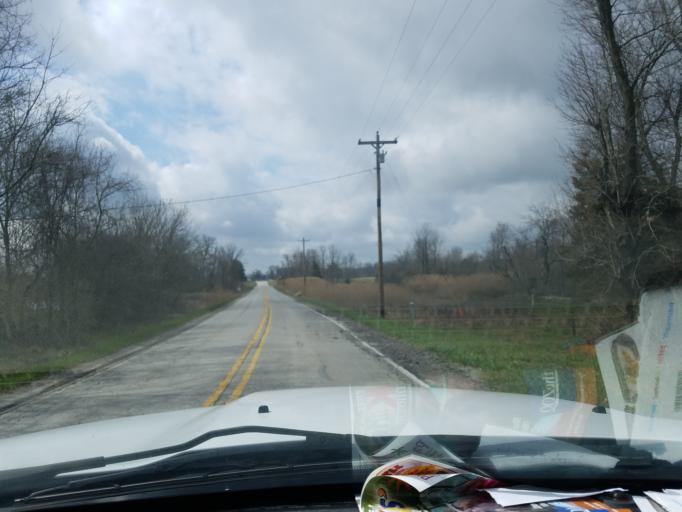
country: US
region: Indiana
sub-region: Sullivan County
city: Farmersburg
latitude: 39.3563
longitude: -87.3065
